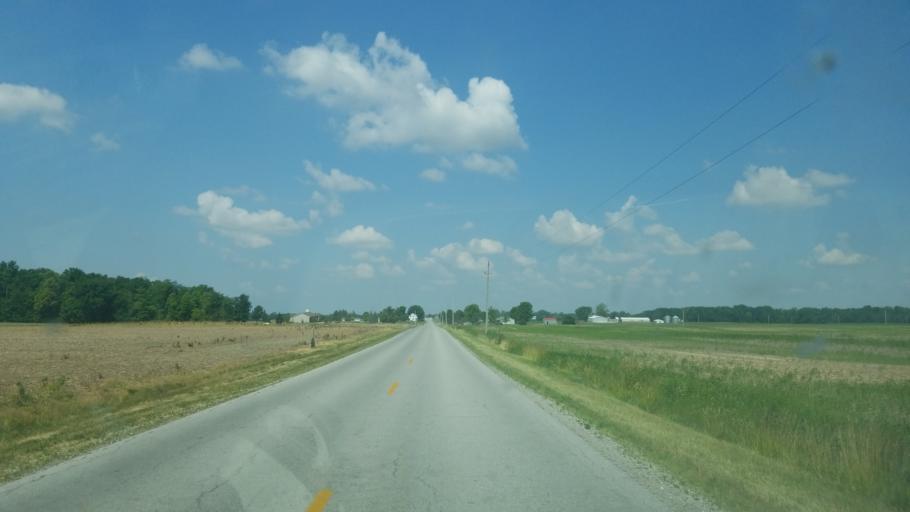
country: US
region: Ohio
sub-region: Auglaize County
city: Wapakoneta
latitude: 40.5702
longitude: -84.1544
